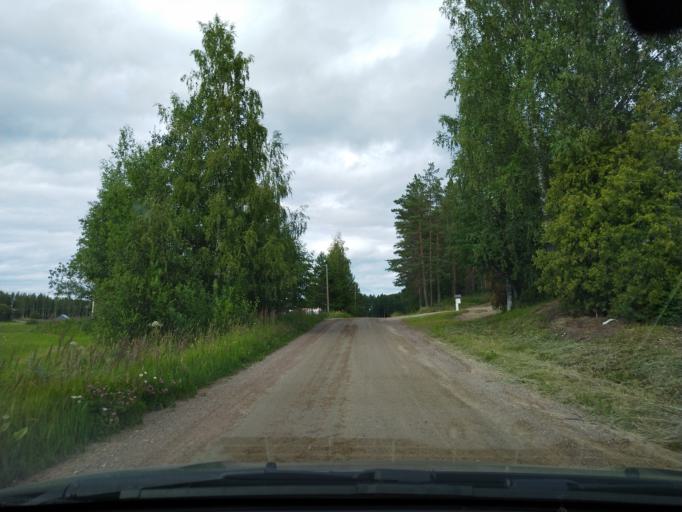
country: FI
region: Kymenlaakso
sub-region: Kouvola
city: Kouvola
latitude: 61.0534
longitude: 26.8695
